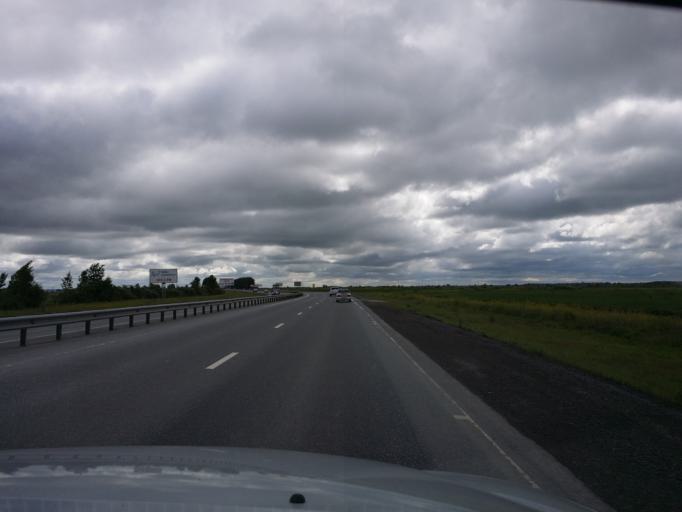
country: RU
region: Tjumen
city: Antipino
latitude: 57.1595
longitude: 65.8149
